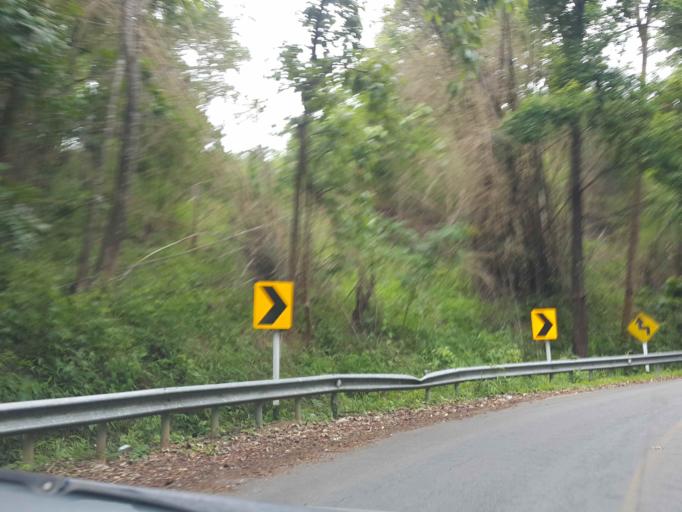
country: TH
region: Chiang Mai
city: Samoeng
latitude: 18.8075
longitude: 98.8137
